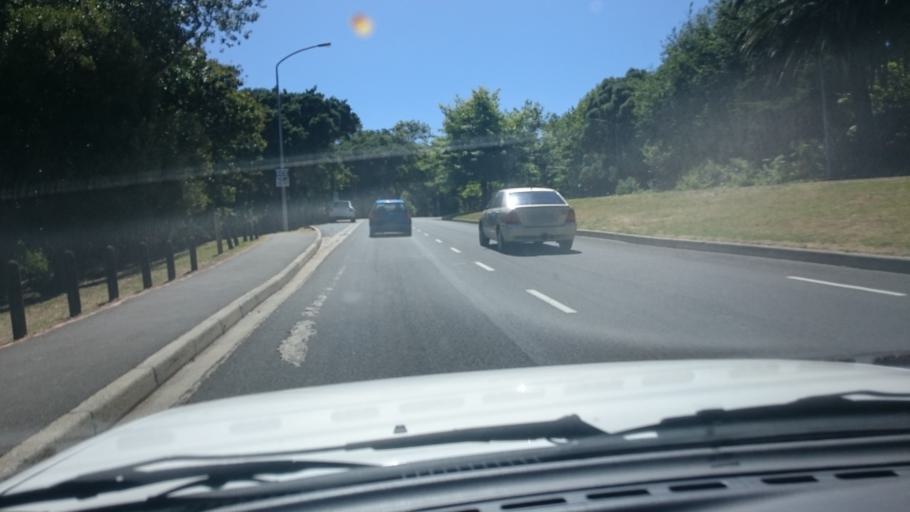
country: ZA
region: Western Cape
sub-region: City of Cape Town
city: Claremont
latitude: -34.0006
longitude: 18.4567
